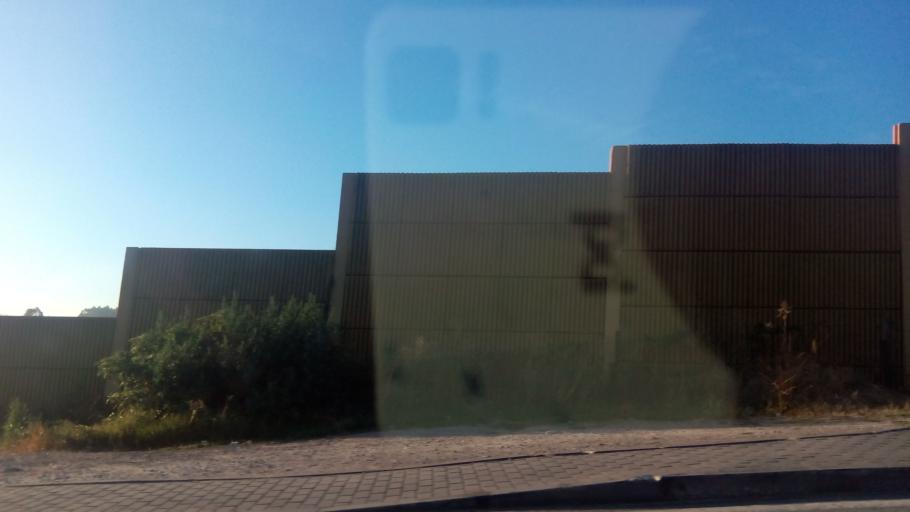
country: PT
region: Porto
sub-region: Paredes
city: Casteloes de Cepeda
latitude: 41.1976
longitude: -8.3505
